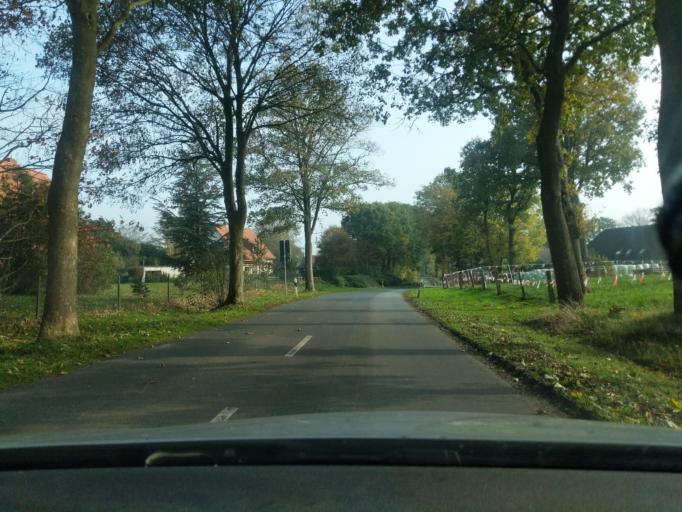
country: DE
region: Lower Saxony
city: Wanna
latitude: 53.7431
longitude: 8.7769
